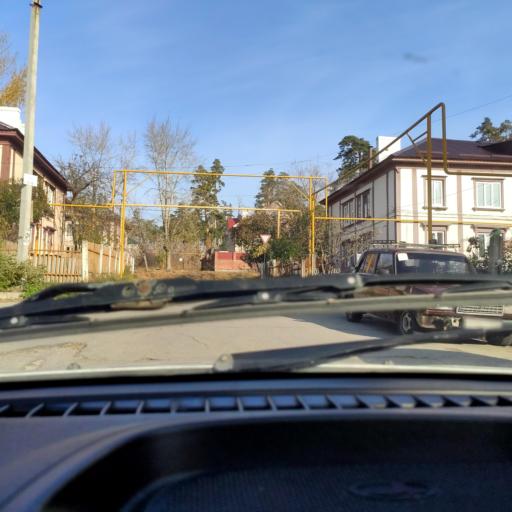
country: RU
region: Samara
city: Tol'yatti
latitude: 53.4755
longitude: 49.3709
